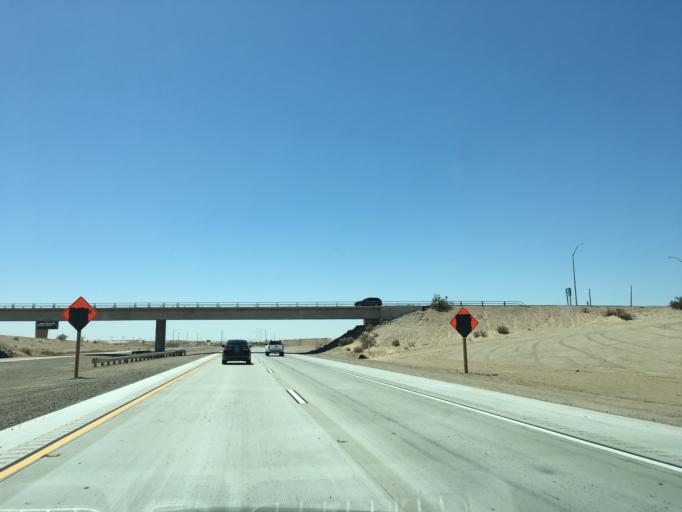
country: MX
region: Baja California
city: Los Algodones
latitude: 32.7434
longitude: -114.7186
